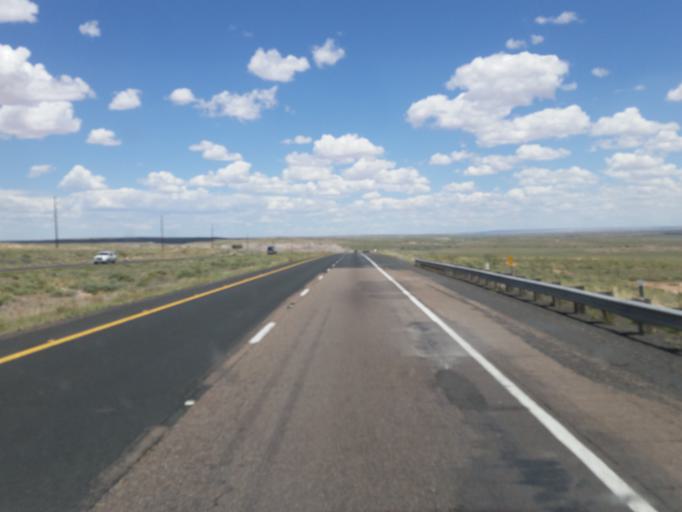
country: US
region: Arizona
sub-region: Navajo County
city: Holbrook
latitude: 34.9892
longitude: -110.0053
